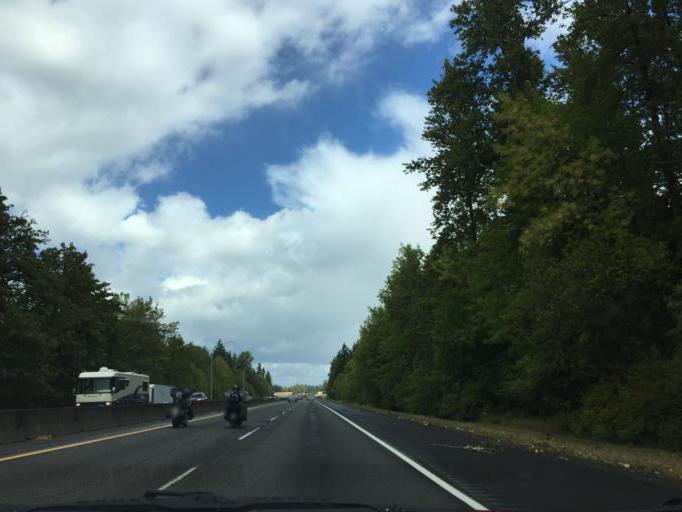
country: US
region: Washington
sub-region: Cowlitz County
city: Castle Rock
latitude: 46.3804
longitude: -122.9045
